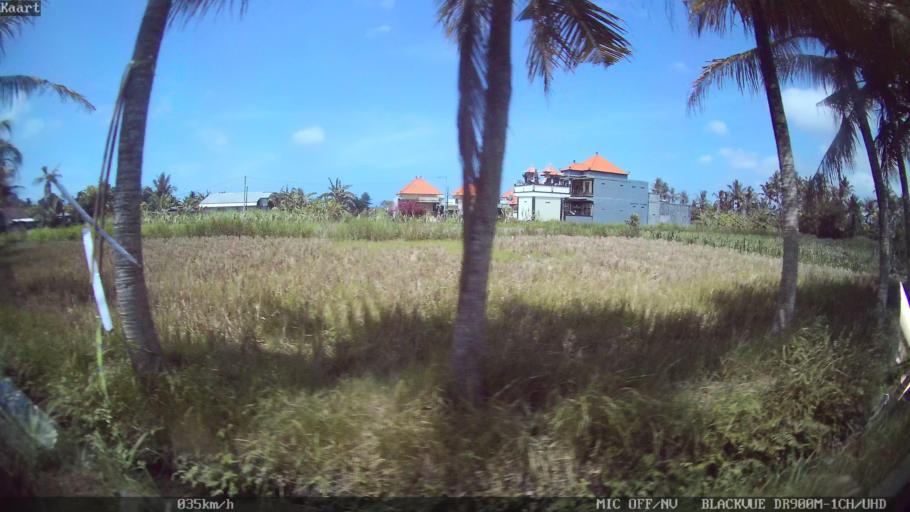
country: ID
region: Bali
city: Banjar Pasekan
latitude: -8.5994
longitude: 115.3065
